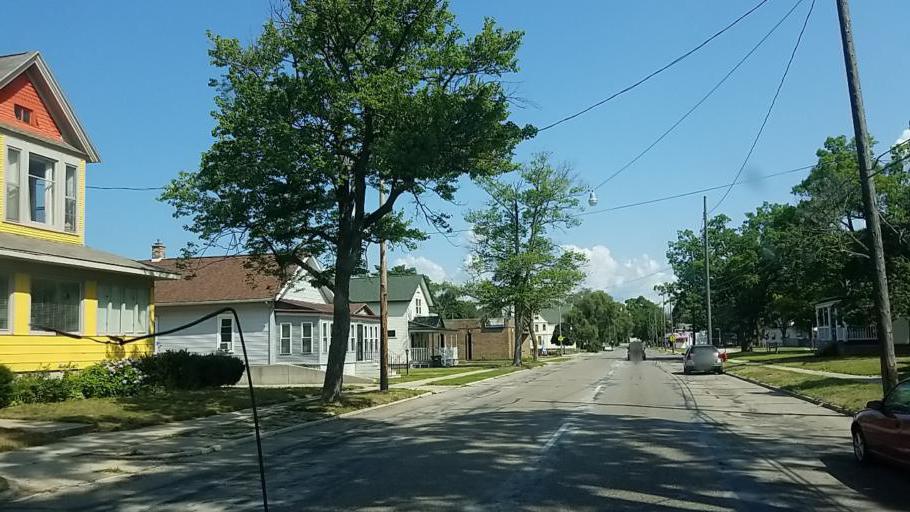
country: US
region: Michigan
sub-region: Muskegon County
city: Muskegon
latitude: 43.2283
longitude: -86.2442
